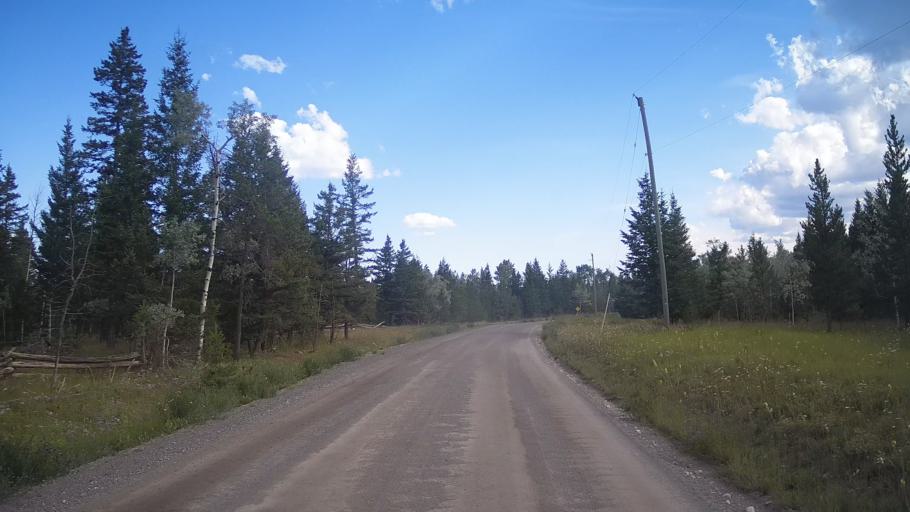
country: CA
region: British Columbia
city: Cache Creek
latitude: 51.1860
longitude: -121.5840
